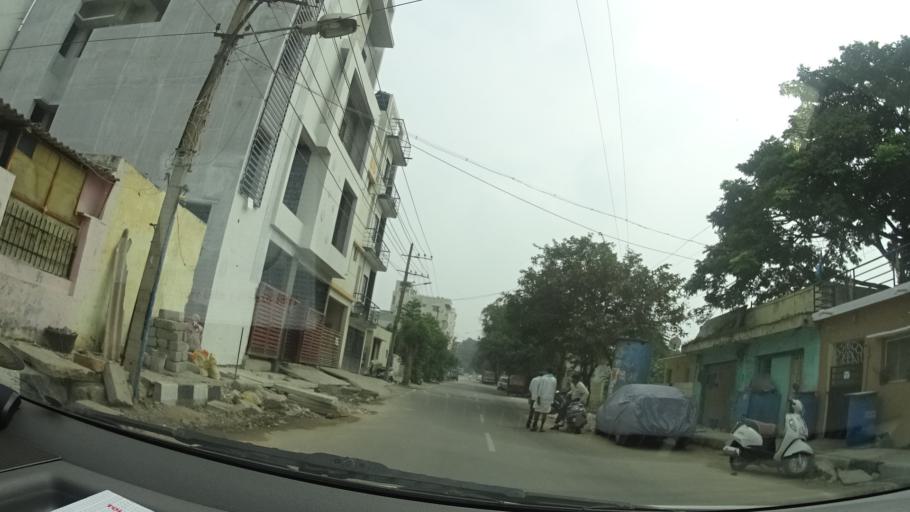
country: IN
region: Karnataka
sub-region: Bangalore Urban
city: Bangalore
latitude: 13.0305
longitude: 77.6264
